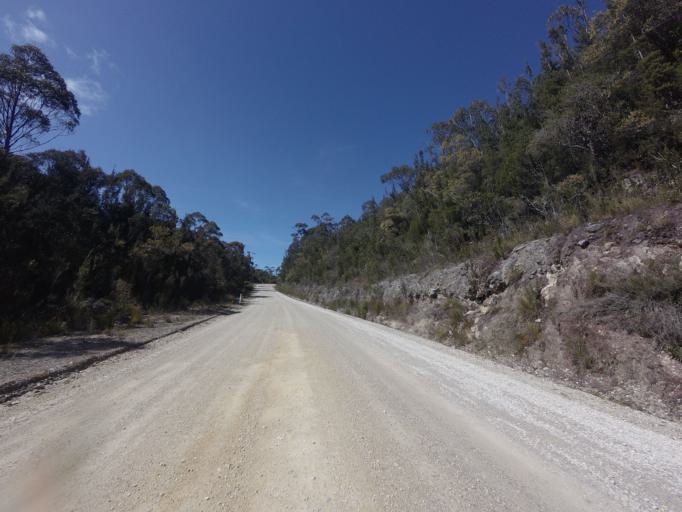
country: AU
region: Tasmania
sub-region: Huon Valley
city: Geeveston
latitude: -42.8168
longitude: 146.3865
